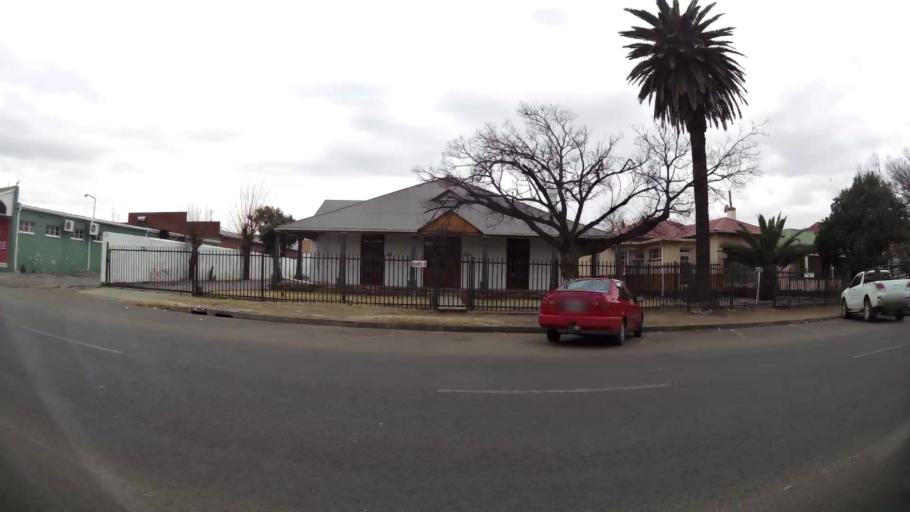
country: ZA
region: Orange Free State
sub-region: Fezile Dabi District Municipality
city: Kroonstad
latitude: -27.6618
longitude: 27.2386
